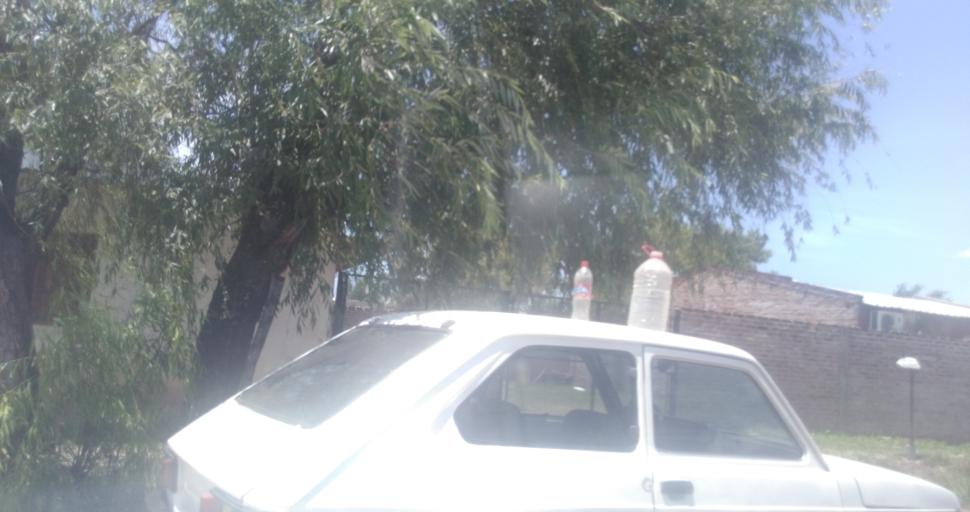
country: AR
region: Chaco
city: Fontana
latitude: -27.4219
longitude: -59.0391
